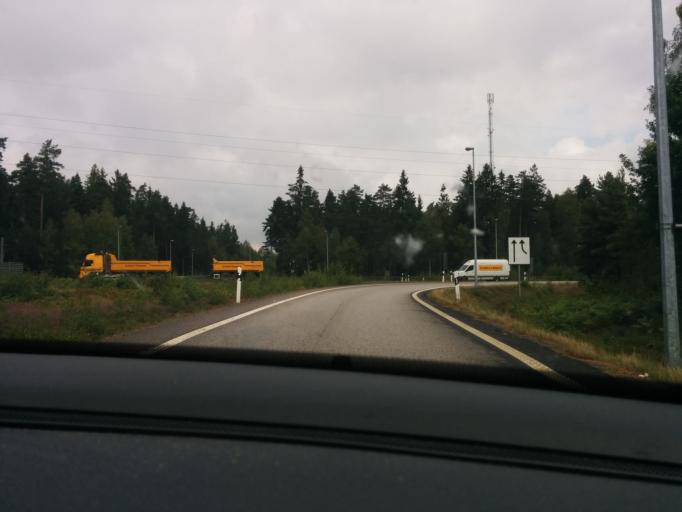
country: SE
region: Kronoberg
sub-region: Vaxjo Kommun
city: Vaexjoe
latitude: 56.9001
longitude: 14.7952
